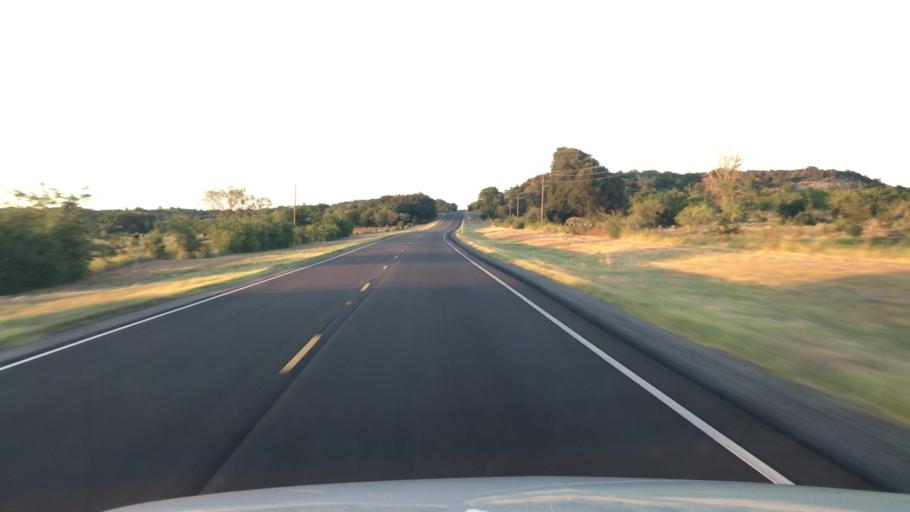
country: US
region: Texas
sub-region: Hamilton County
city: Hico
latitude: 32.0918
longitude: -97.9707
